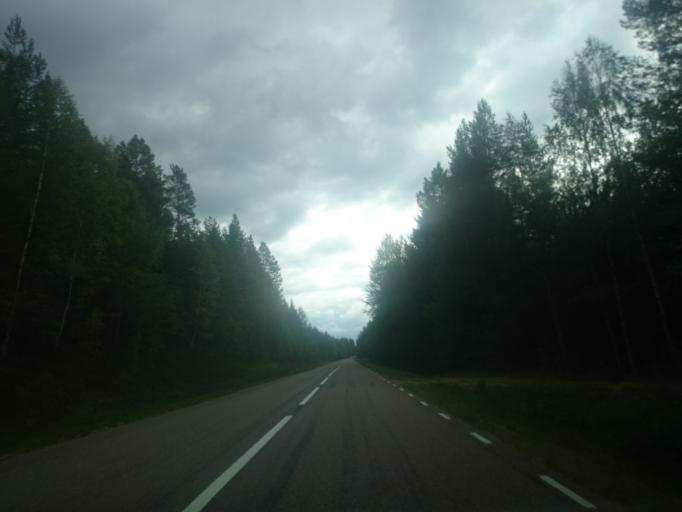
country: SE
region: Jaemtland
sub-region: Harjedalens Kommun
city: Sveg
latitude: 62.2885
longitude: 13.8133
